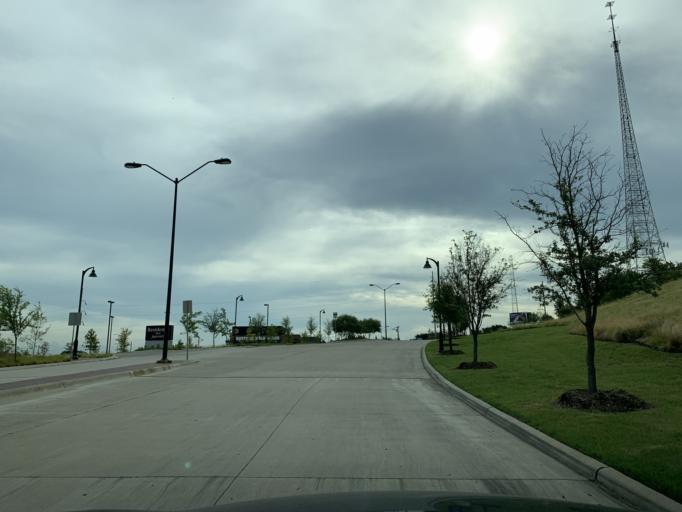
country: US
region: Texas
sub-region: Dallas County
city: Cockrell Hill
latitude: 32.7655
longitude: -96.8759
